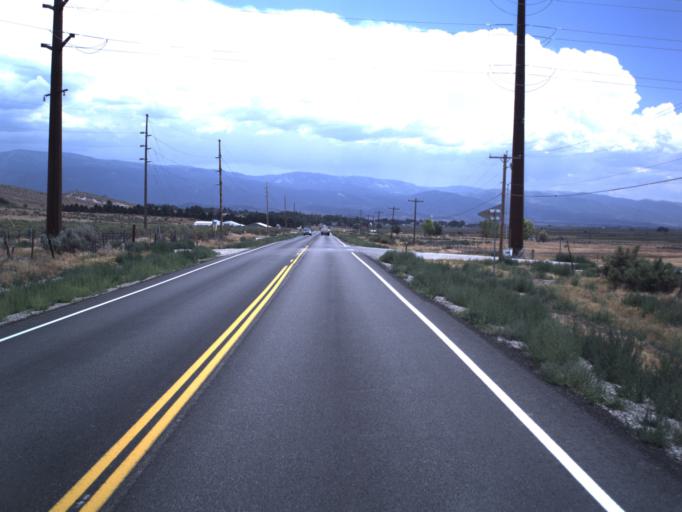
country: US
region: Utah
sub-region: Sanpete County
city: Moroni
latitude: 39.5496
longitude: -111.5993
